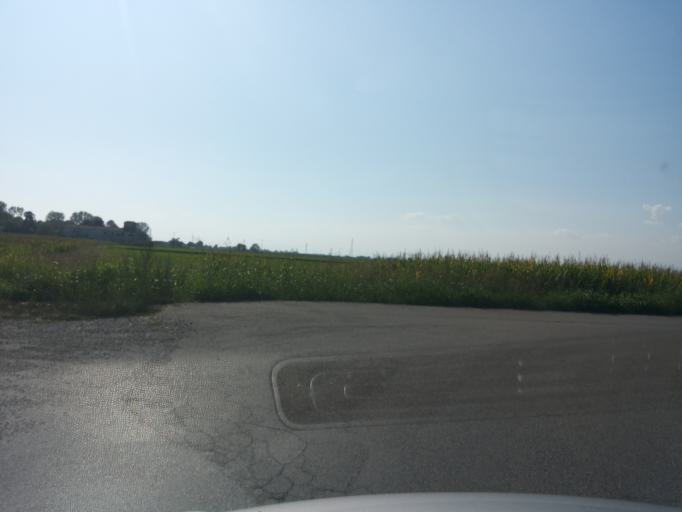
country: IT
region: Piedmont
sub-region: Provincia di Vercelli
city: Vercelli
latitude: 45.3353
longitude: 8.4011
